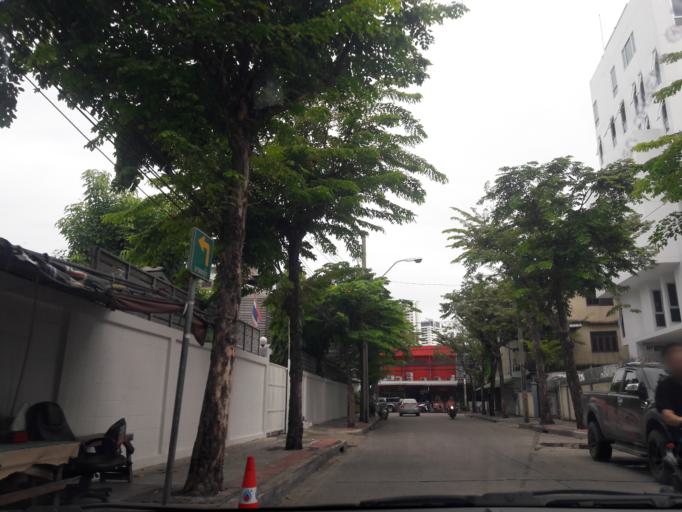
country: TH
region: Bangkok
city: Khlong San
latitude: 13.7270
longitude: 100.4994
